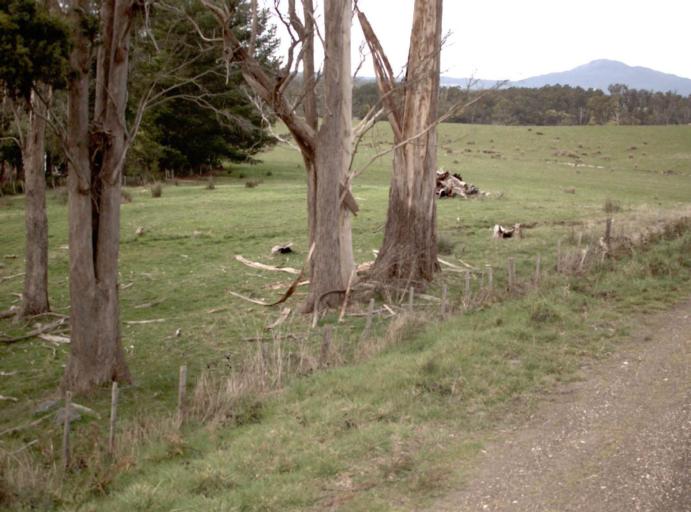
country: AU
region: Tasmania
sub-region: Launceston
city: Mayfield
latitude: -41.2077
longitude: 147.1182
